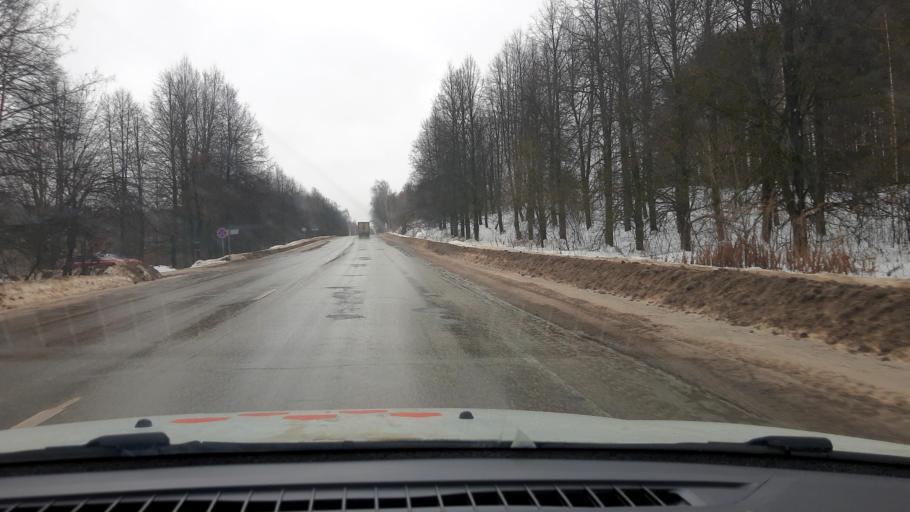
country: RU
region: Nizjnij Novgorod
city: Pavlovo
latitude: 55.9670
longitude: 43.1235
